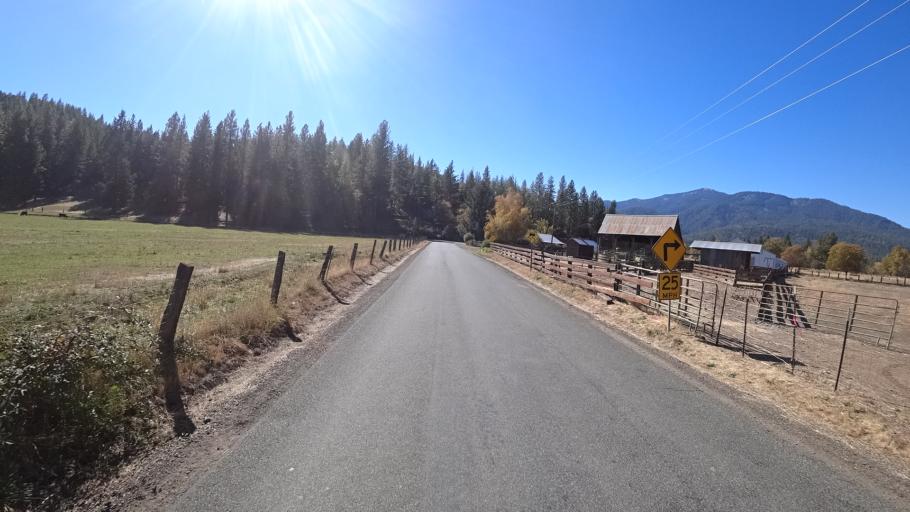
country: US
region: California
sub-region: Siskiyou County
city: Yreka
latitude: 41.6257
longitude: -122.9609
